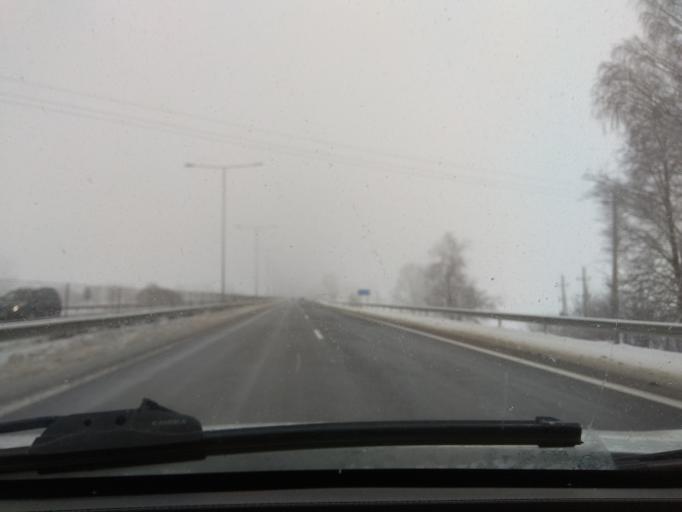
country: LT
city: Kaisiadorys
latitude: 54.8433
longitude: 24.3371
